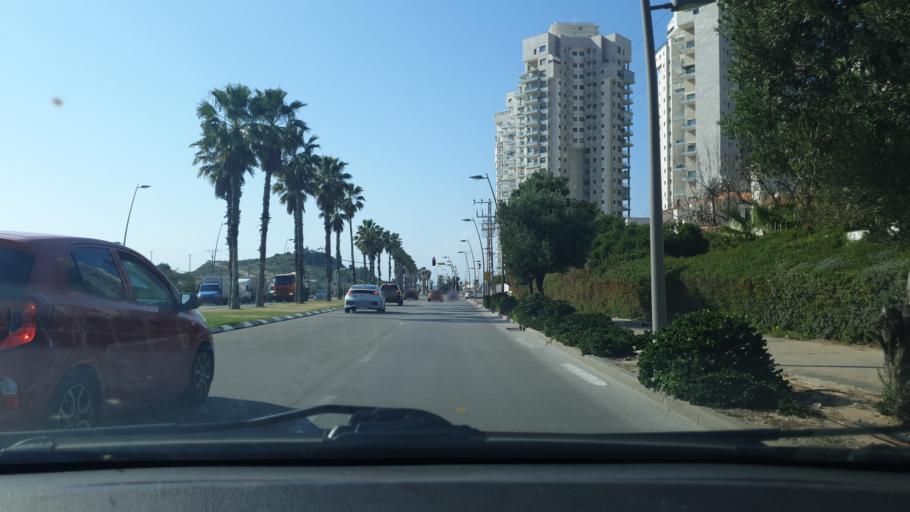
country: IL
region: Tel Aviv
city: Bat Yam
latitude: 31.9953
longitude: 34.7383
